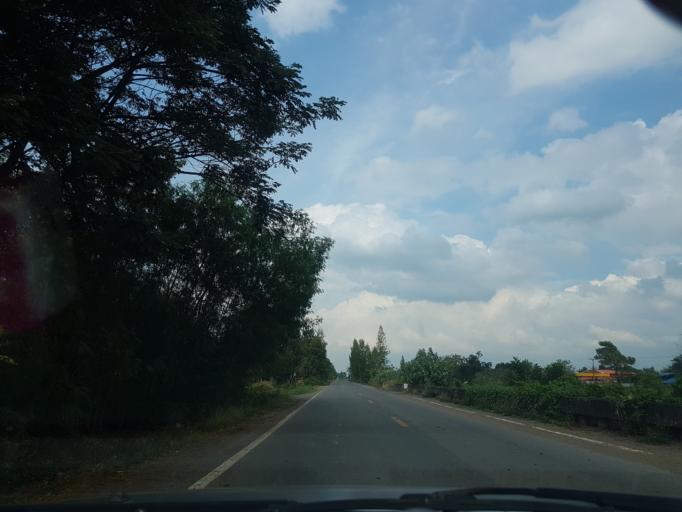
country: TH
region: Pathum Thani
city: Nong Suea
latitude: 14.2099
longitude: 100.8915
